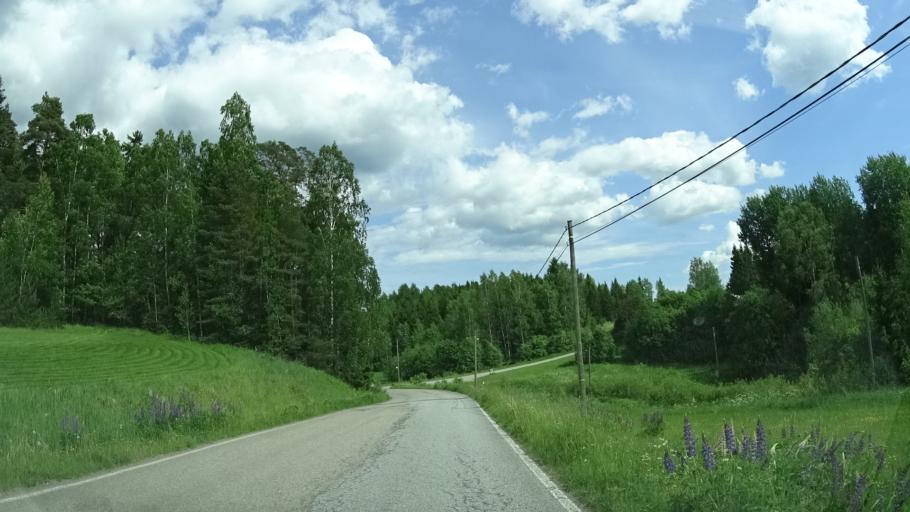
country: FI
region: Uusimaa
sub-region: Helsinki
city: Siuntio
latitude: 60.1928
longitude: 24.2139
